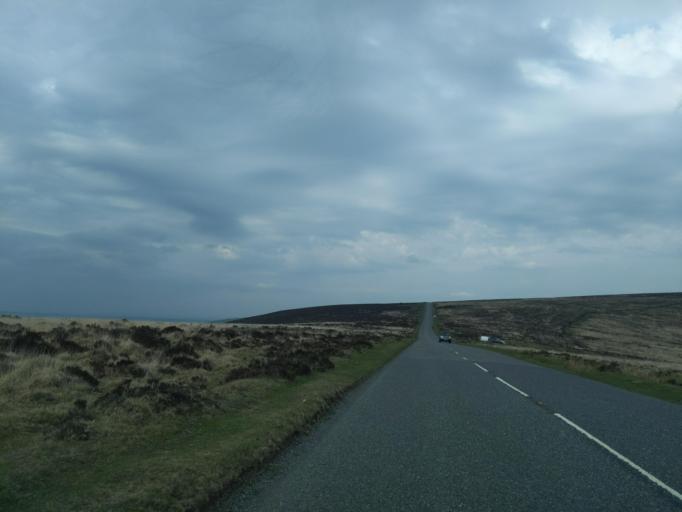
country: GB
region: England
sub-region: Devon
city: Ashburton
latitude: 50.6180
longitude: -3.8692
